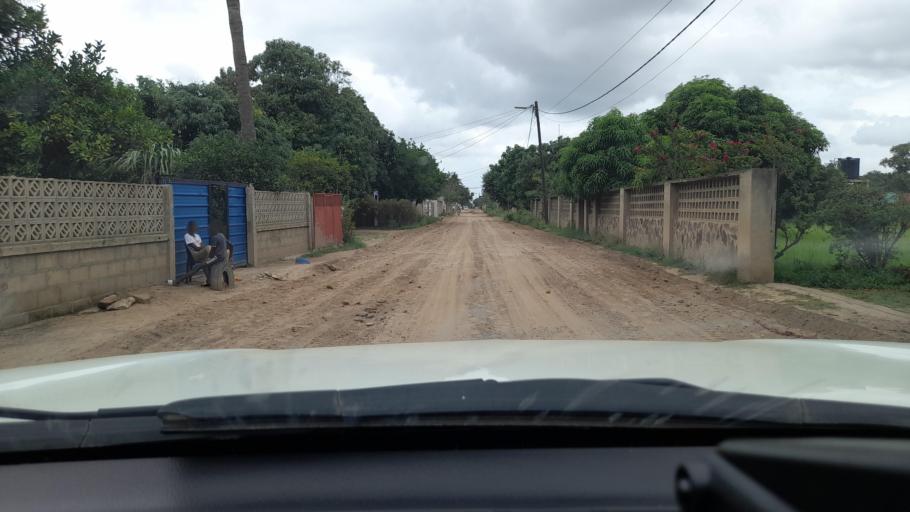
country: MZ
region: Maputo
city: Matola
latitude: -25.9012
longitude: 32.4851
